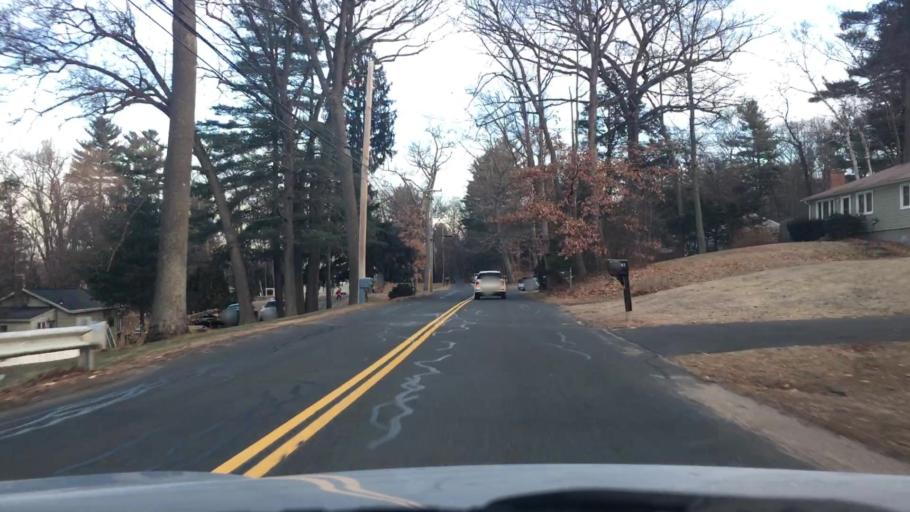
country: US
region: Massachusetts
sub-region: Hampden County
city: Westfield
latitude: 42.0900
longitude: -72.7128
